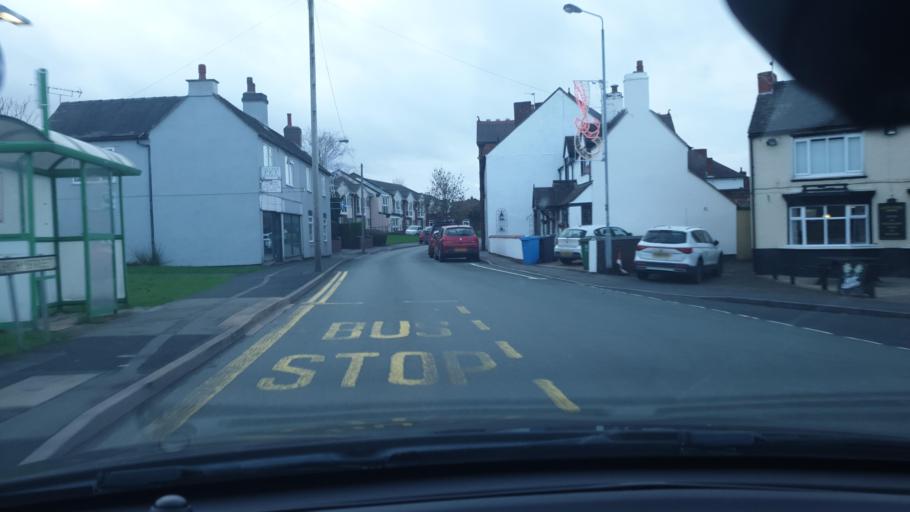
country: GB
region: England
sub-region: Staffordshire
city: Great Wyrley
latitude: 52.6602
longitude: -2.0362
